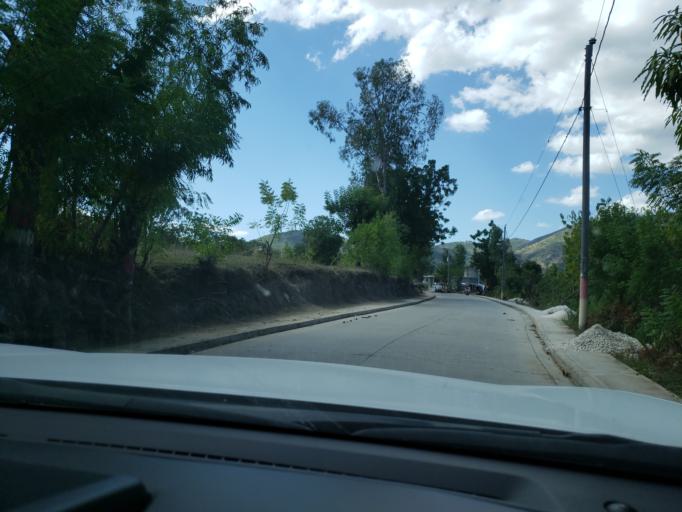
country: HT
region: Grandans
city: Anse-a-Veau
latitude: 18.4497
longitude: -73.3843
